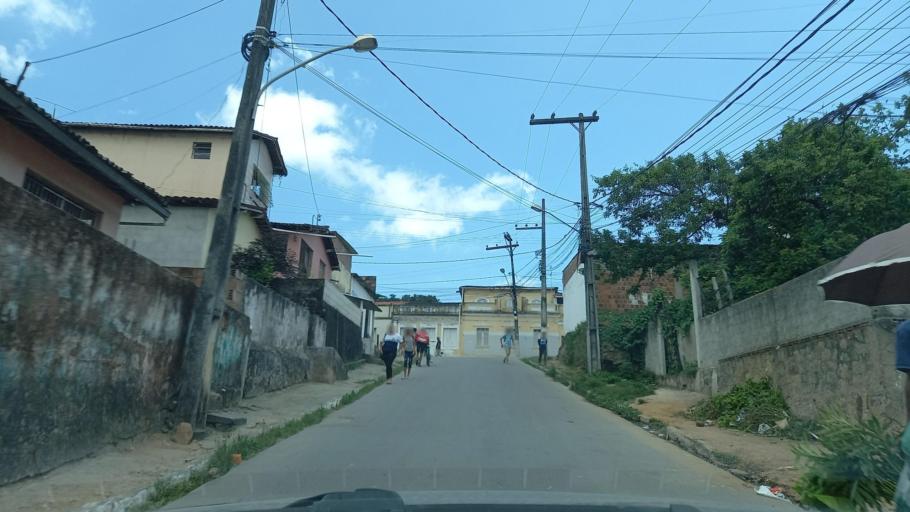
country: BR
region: Pernambuco
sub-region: Jaboatao Dos Guararapes
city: Jaboatao
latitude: -8.1735
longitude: -35.0001
